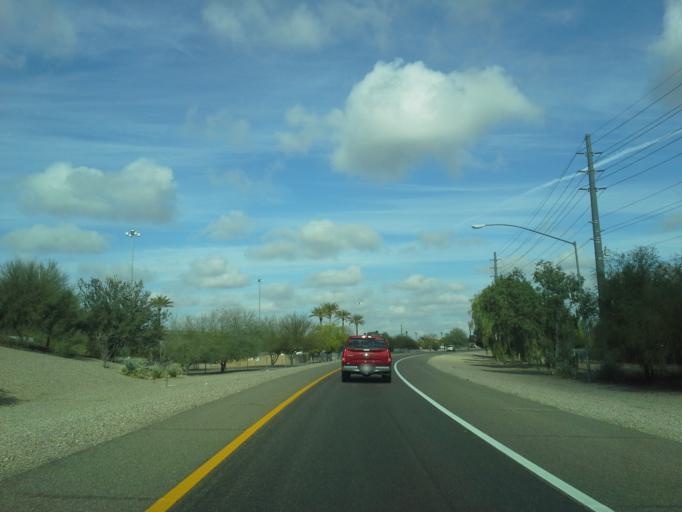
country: US
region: Arizona
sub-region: Maricopa County
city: Sun City
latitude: 33.5986
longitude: -112.2550
